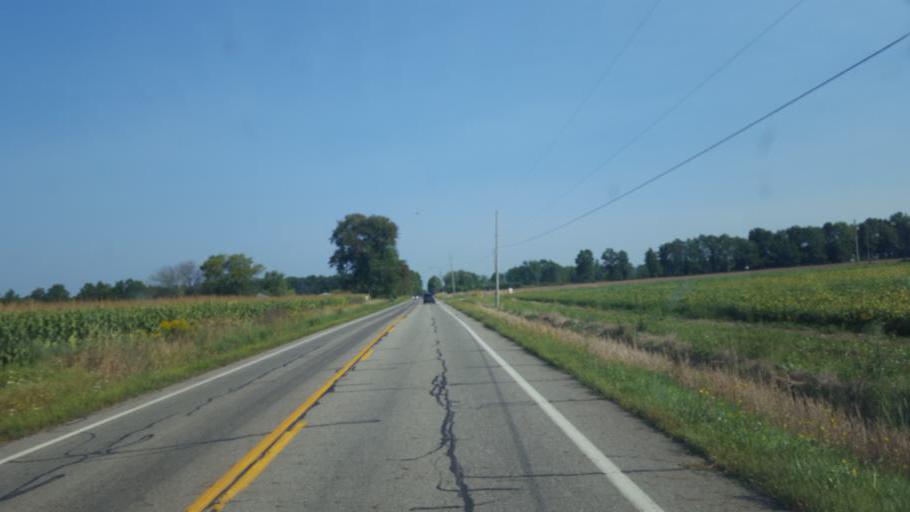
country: US
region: Ohio
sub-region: Ashtabula County
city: Orwell
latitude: 41.4787
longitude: -80.8683
